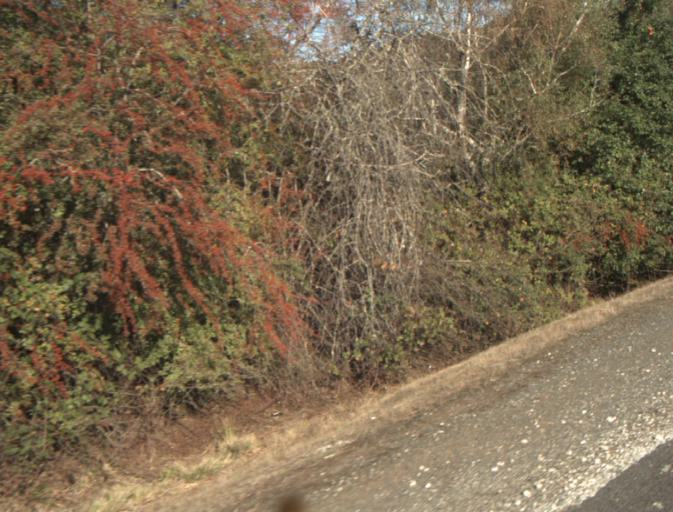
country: AU
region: Tasmania
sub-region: Launceston
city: Mayfield
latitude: -41.2785
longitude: 147.2202
